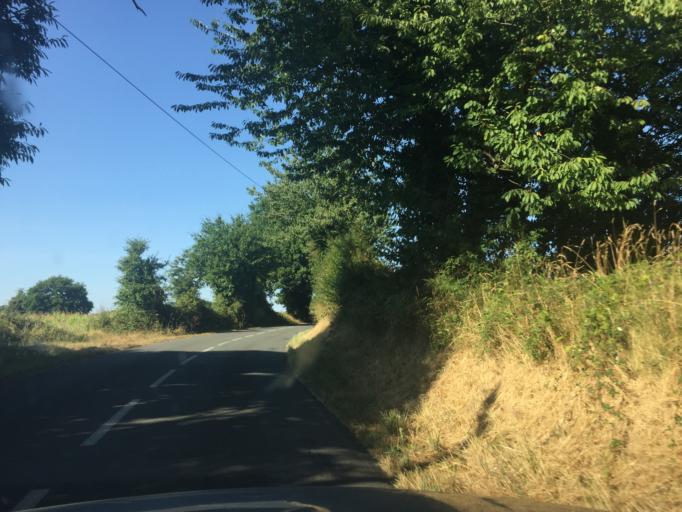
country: FR
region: Poitou-Charentes
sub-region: Departement des Deux-Sevres
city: Lezay
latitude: 46.1905
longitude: -0.0394
